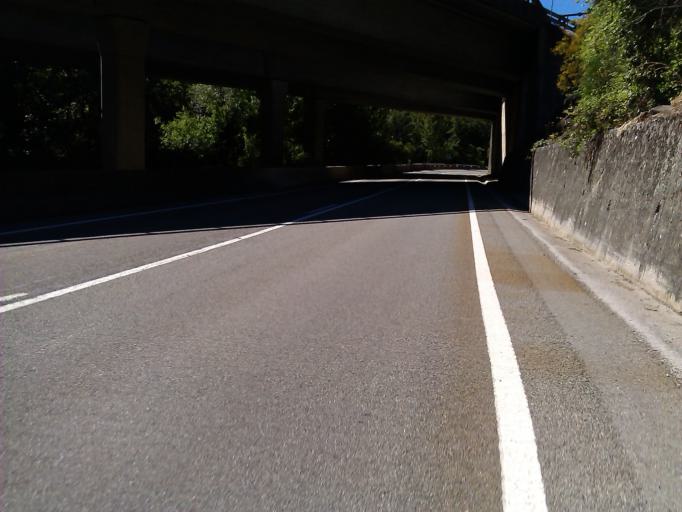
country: ES
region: Castille and Leon
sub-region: Provincia de Leon
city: Trabadelo
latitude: 42.6327
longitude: -6.8513
